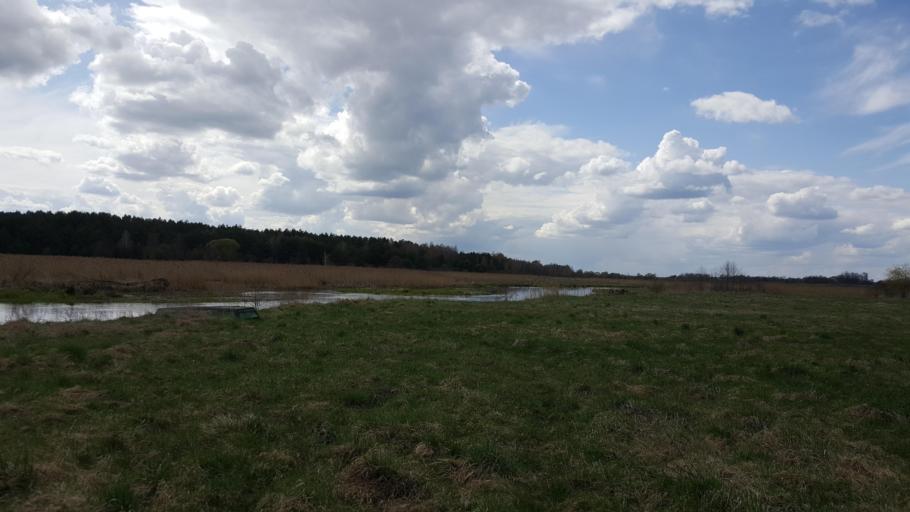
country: BY
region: Brest
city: Kamyanyets
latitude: 52.3491
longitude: 23.7092
